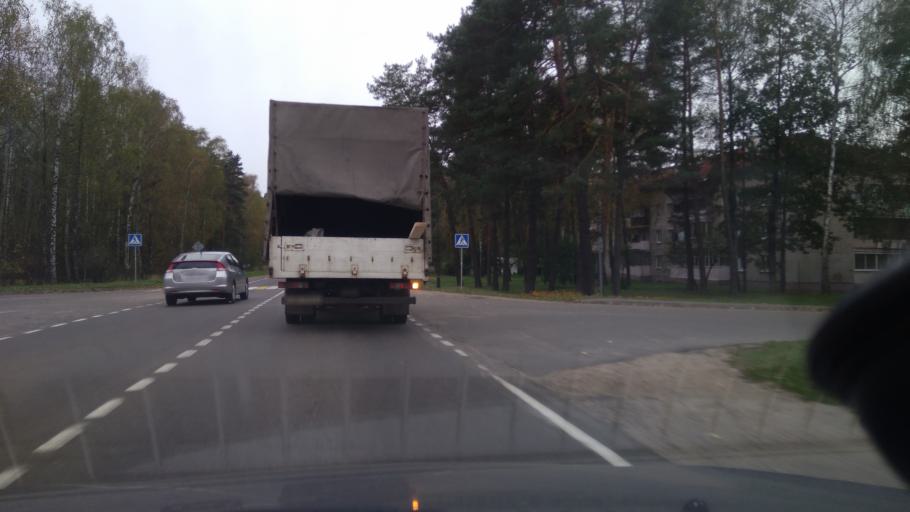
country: BY
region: Minsk
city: Svislach
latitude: 53.6437
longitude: 27.9127
